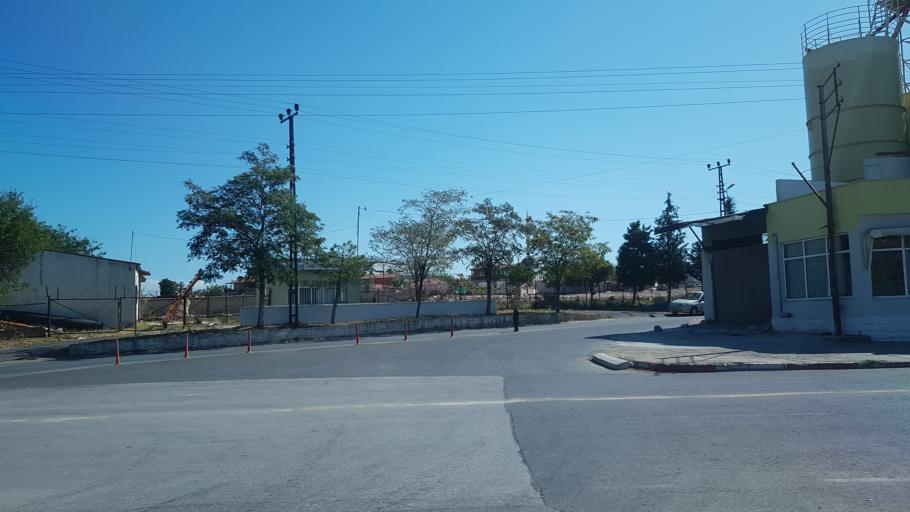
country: TR
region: Kirklareli
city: Kirklareli
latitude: 41.7459
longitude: 27.2197
